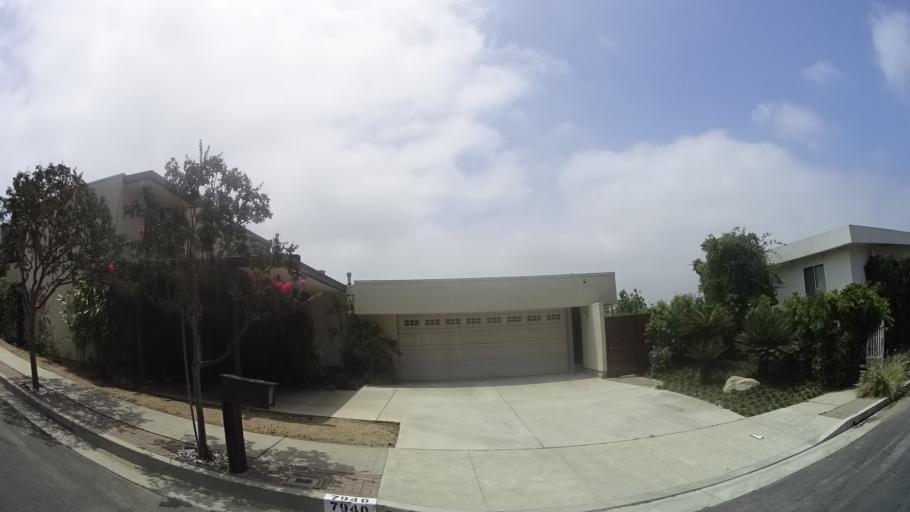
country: US
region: California
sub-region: Los Angeles County
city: West Hollywood
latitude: 34.1123
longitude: -118.3674
